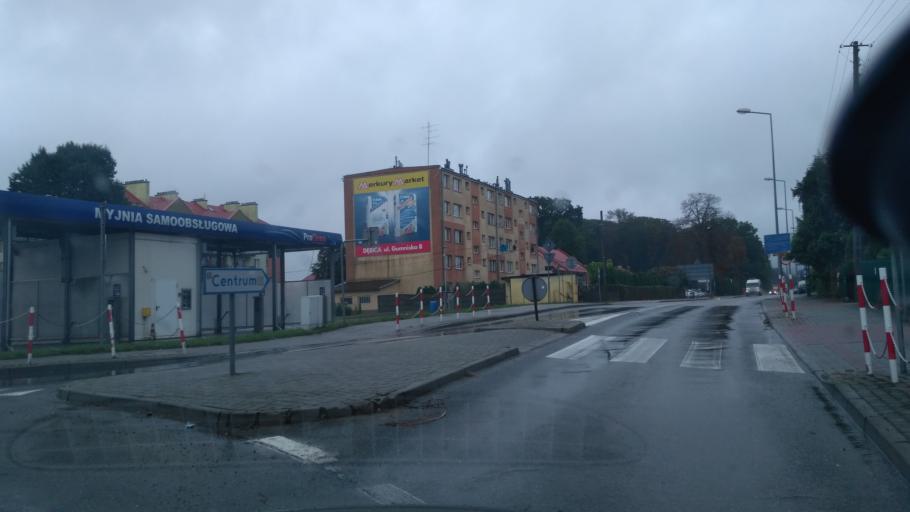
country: PL
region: Subcarpathian Voivodeship
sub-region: Powiat debicki
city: Debica
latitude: 50.0631
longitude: 21.4051
